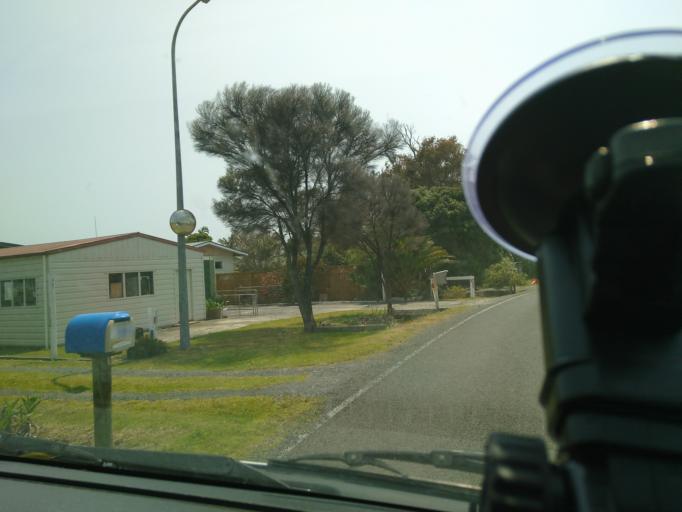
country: NZ
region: Northland
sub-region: Far North District
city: Kaitaia
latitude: -34.8157
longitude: 173.1167
